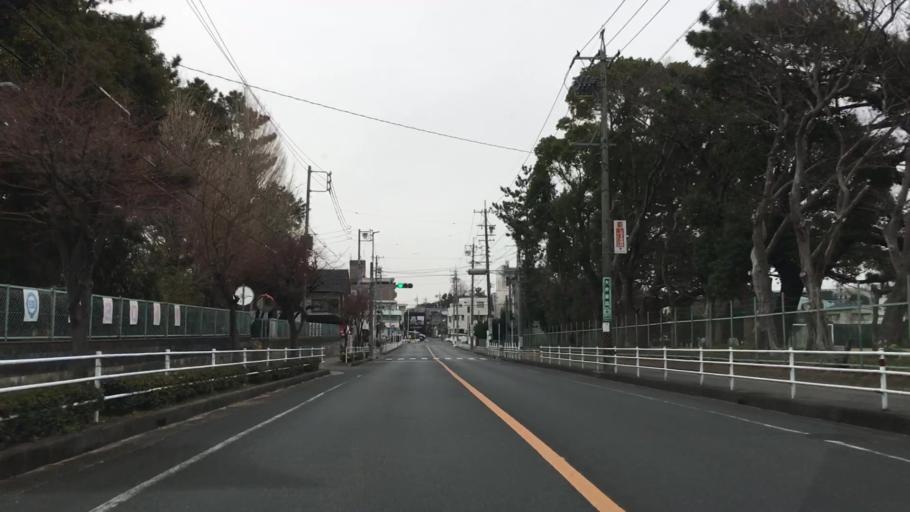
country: JP
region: Aichi
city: Toyohashi
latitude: 34.7415
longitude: 137.3828
